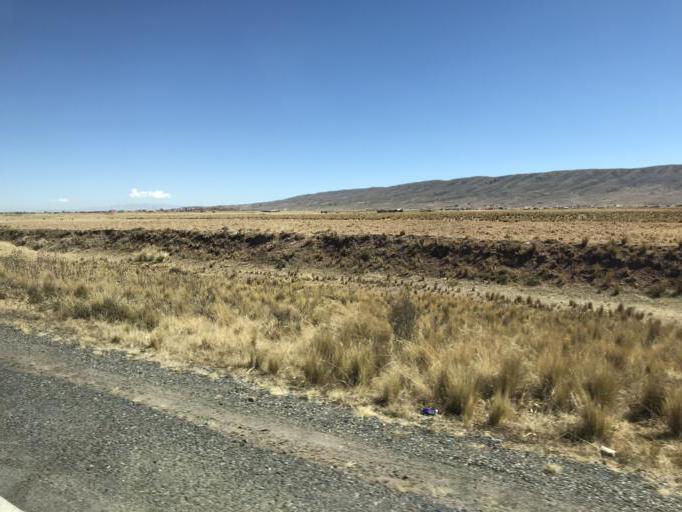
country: BO
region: La Paz
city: Tiahuanaco
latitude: -16.5676
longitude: -68.6531
